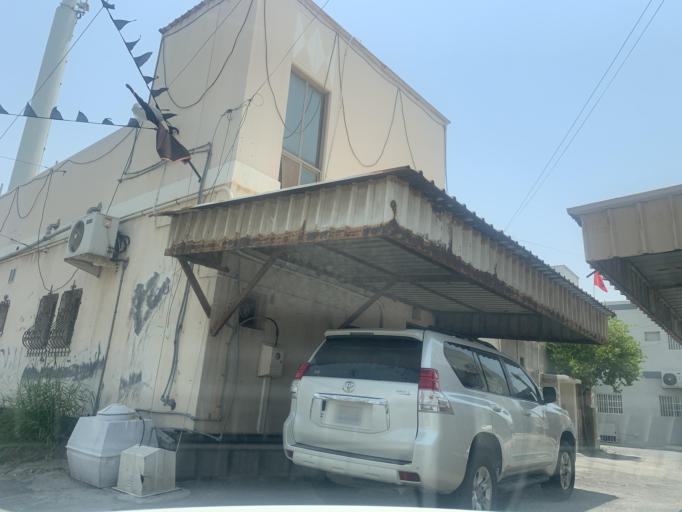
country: BH
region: Central Governorate
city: Madinat Hamad
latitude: 26.1432
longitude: 50.4613
